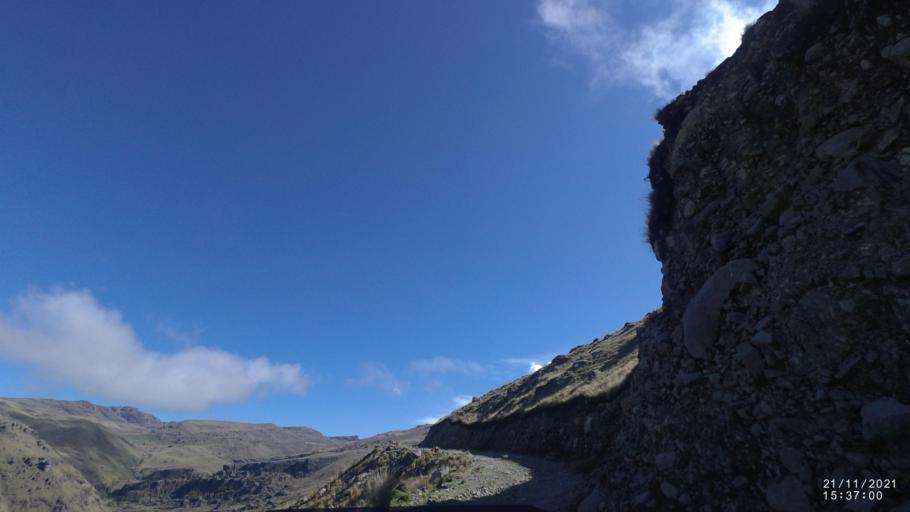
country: BO
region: Cochabamba
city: Cochabamba
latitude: -16.9619
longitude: -66.2664
